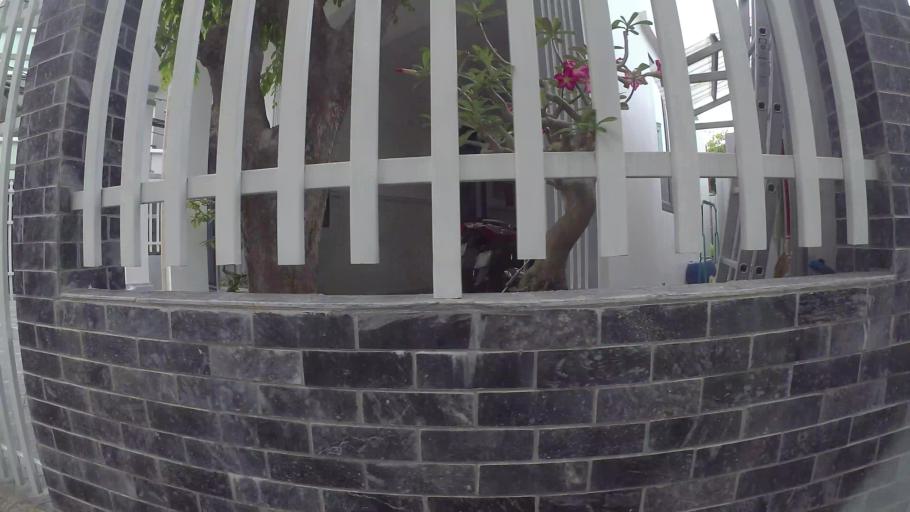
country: VN
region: Da Nang
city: Da Nang
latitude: 16.0839
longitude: 108.2195
